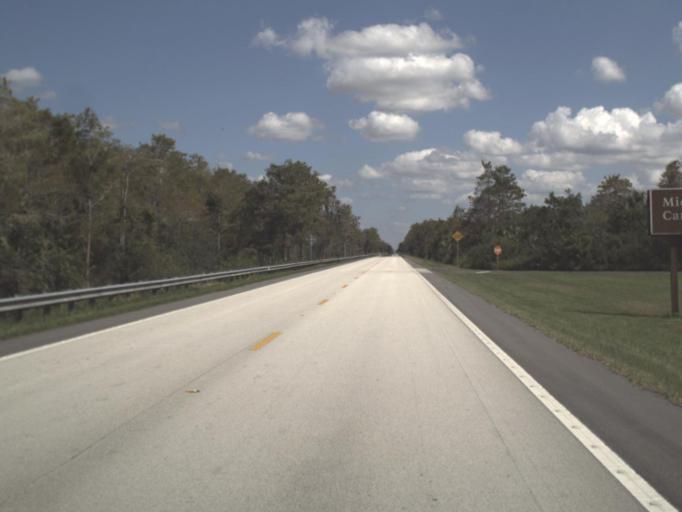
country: US
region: Florida
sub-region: Miami-Dade County
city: Kendall West
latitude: 25.8524
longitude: -80.9895
